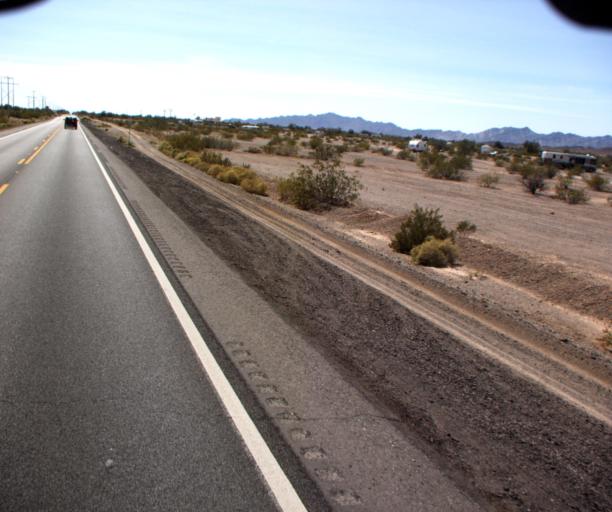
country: US
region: Arizona
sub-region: La Paz County
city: Quartzsite
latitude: 33.6554
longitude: -114.2171
